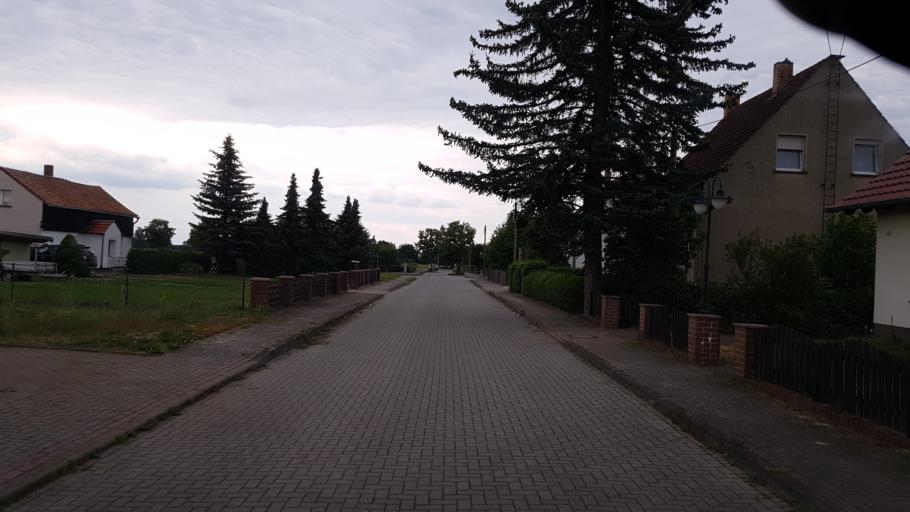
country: DE
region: Saxony-Anhalt
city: Holzdorf
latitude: 51.8173
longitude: 13.2294
